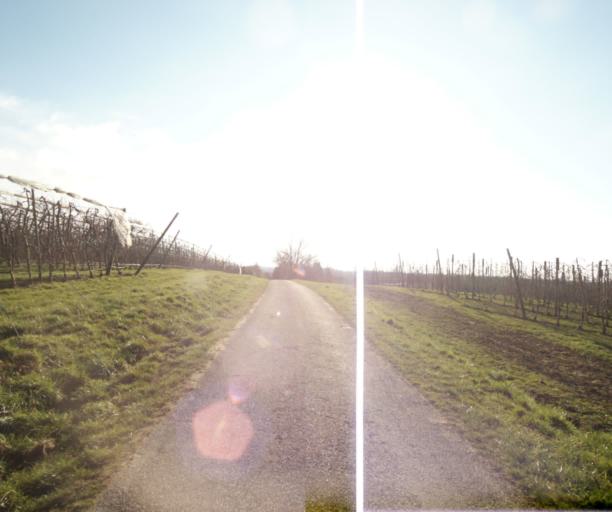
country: FR
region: Midi-Pyrenees
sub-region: Departement du Tarn-et-Garonne
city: Moissac
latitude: 44.1334
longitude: 1.0542
